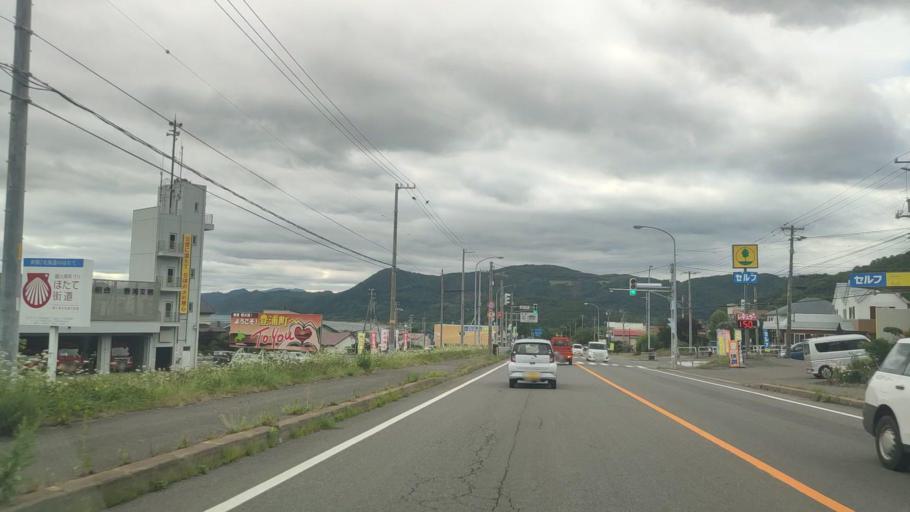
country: JP
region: Hokkaido
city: Date
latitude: 42.5809
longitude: 140.7181
